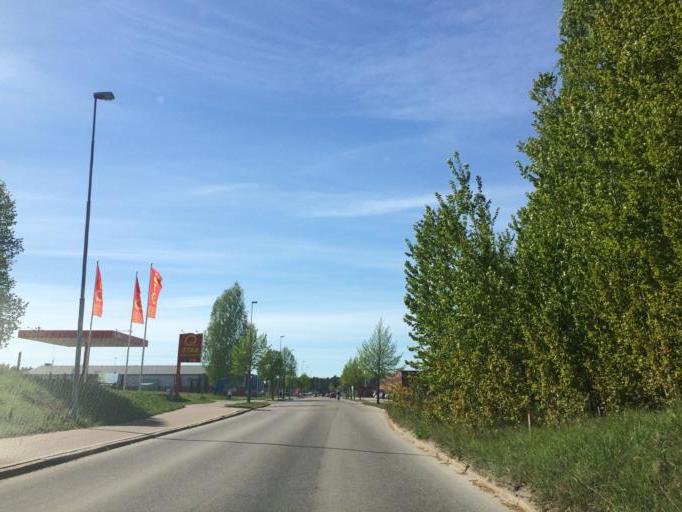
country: SE
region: Soedermanland
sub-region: Katrineholms Kommun
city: Katrineholm
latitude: 58.9954
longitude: 16.1943
